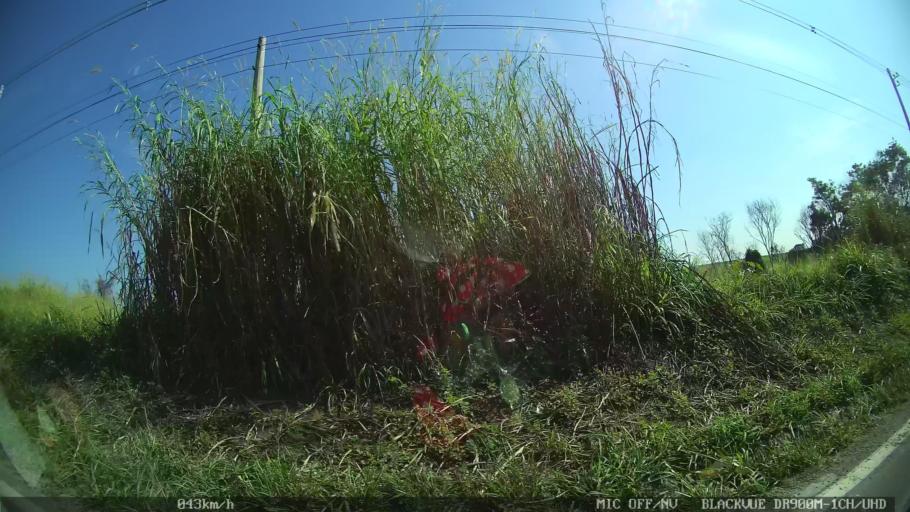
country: BR
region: Sao Paulo
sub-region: Valinhos
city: Valinhos
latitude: -23.0154
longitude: -47.0949
